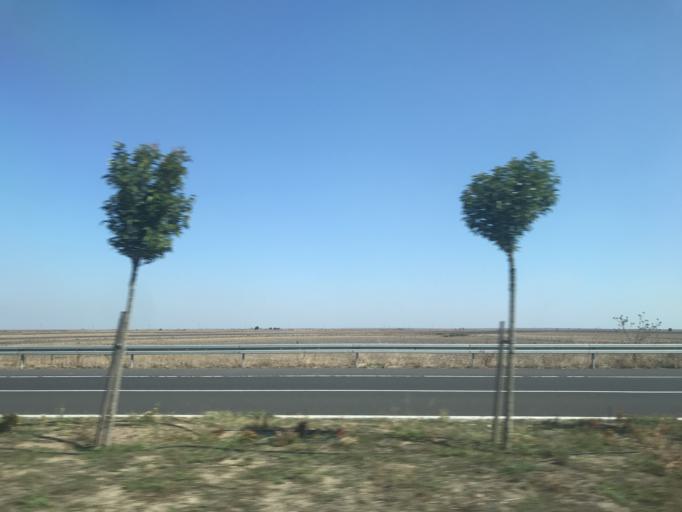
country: TR
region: Tekirdag
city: Muratli
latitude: 41.1942
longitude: 27.5389
